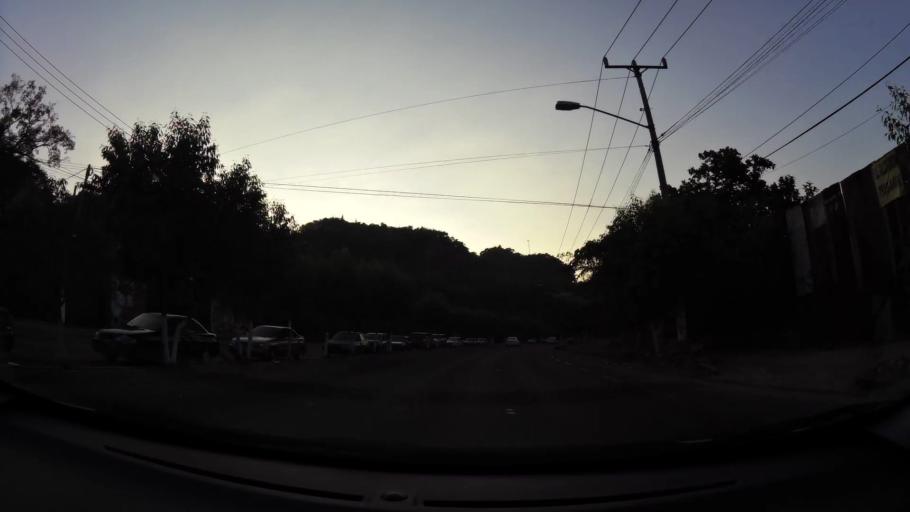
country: SV
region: San Salvador
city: San Salvador
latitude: 13.6790
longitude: -89.2112
